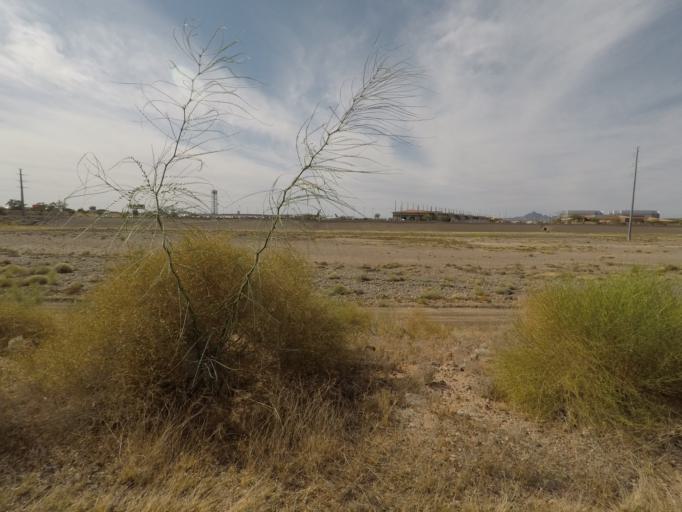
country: US
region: Arizona
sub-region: Maricopa County
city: Phoenix
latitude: 33.4196
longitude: -112.0144
